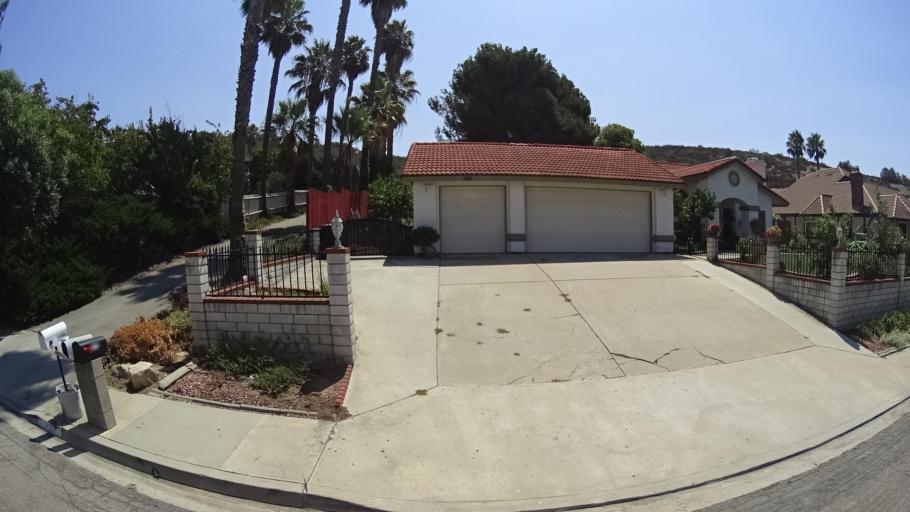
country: US
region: California
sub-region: San Diego County
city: Bonsall
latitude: 33.2793
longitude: -117.2211
